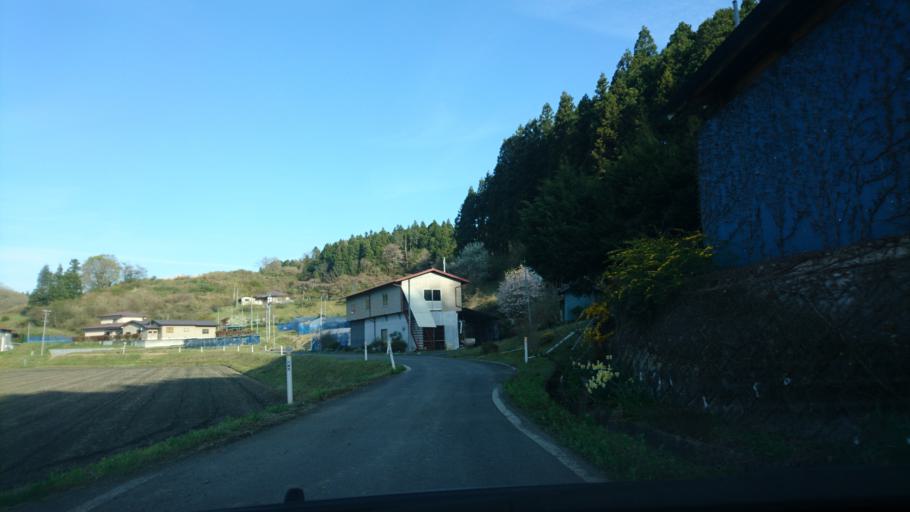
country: JP
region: Iwate
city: Ichinoseki
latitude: 38.8958
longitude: 141.2974
